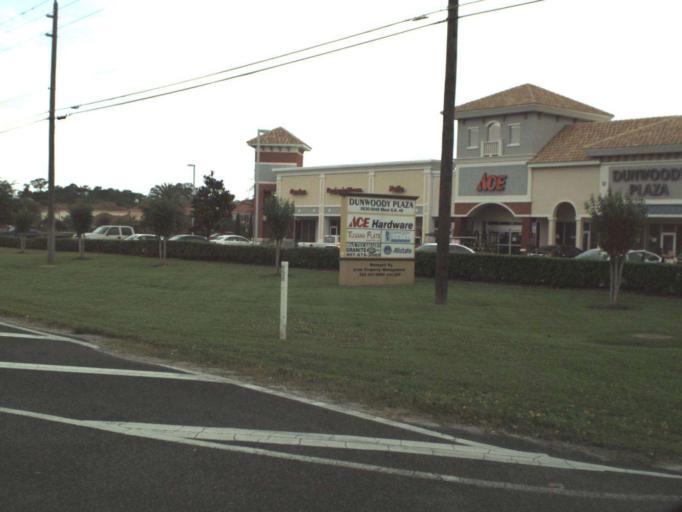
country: US
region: Florida
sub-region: Seminole County
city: Heathrow
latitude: 28.8114
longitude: -81.3466
